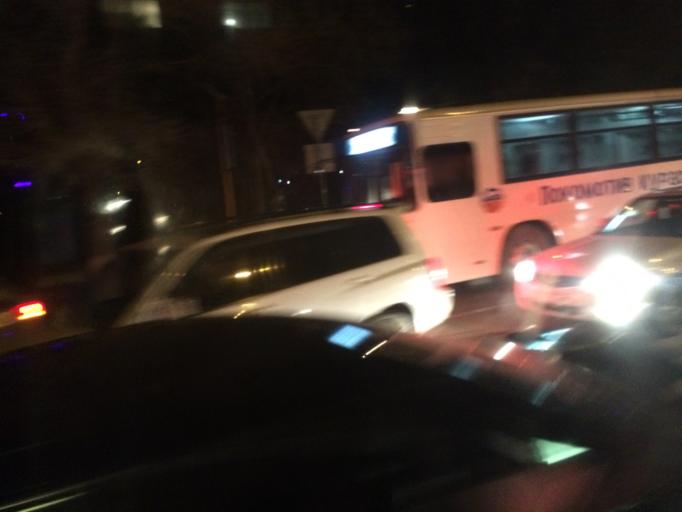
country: KZ
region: Astana Qalasy
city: Astana
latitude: 51.1664
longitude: 71.4513
